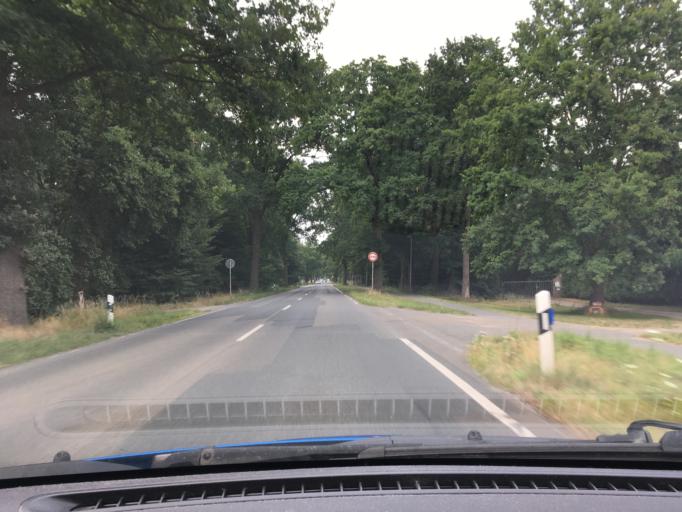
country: DE
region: Lower Saxony
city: Adelheidsdorf
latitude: 52.5784
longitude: 10.0639
